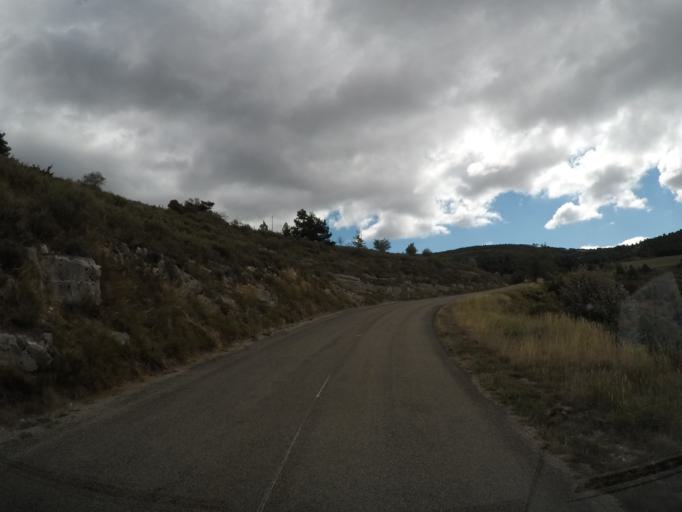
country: FR
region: Provence-Alpes-Cote d'Azur
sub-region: Departement du Vaucluse
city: Sault
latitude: 44.1798
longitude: 5.5102
